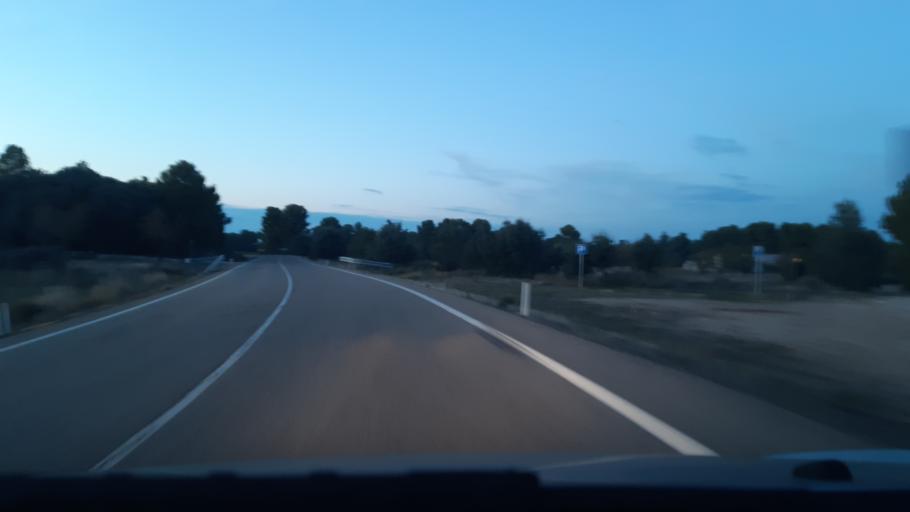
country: ES
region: Aragon
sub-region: Provincia de Teruel
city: Lledo
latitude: 40.9520
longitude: 0.2235
